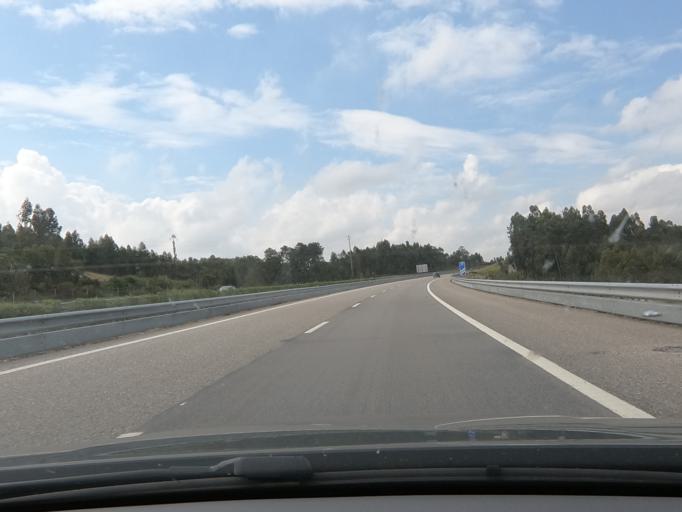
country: PT
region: Leiria
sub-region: Leiria
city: Amor
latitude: 39.7549
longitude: -8.8761
